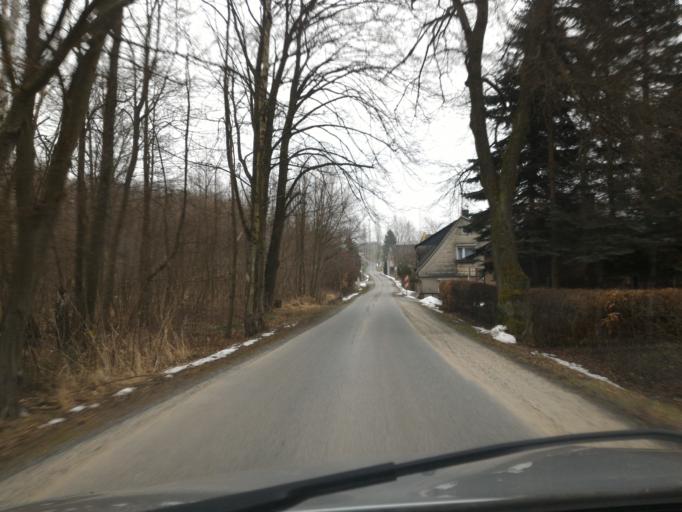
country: DE
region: Saxony
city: Neugersdorf
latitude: 50.9638
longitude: 14.6181
